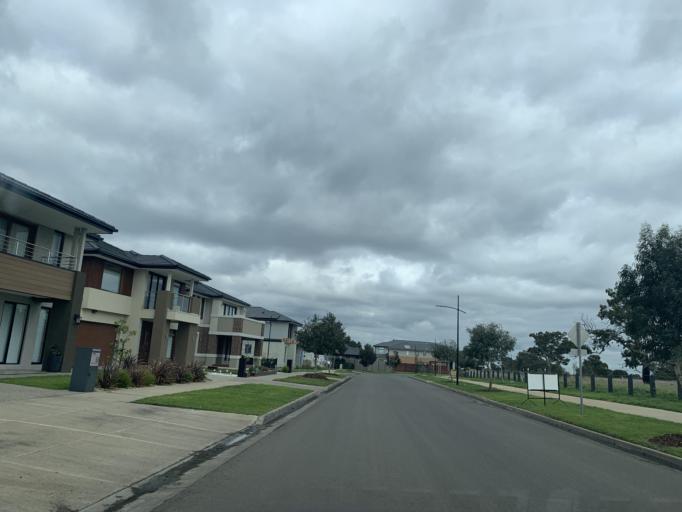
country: AU
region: Victoria
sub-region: Hume
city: Craigieburn
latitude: -37.6003
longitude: 144.9967
